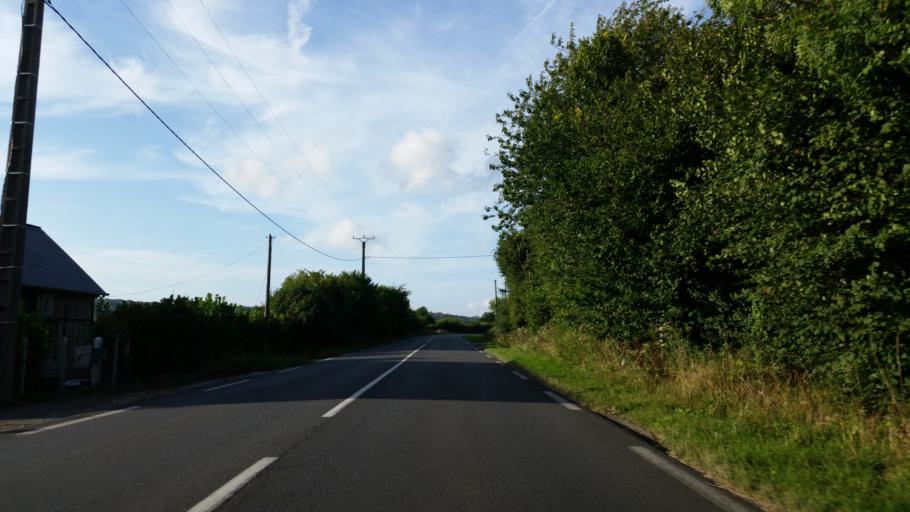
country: FR
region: Lower Normandy
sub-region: Departement du Calvados
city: Saint-Gatien-des-Bois
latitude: 49.3122
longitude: 0.1841
